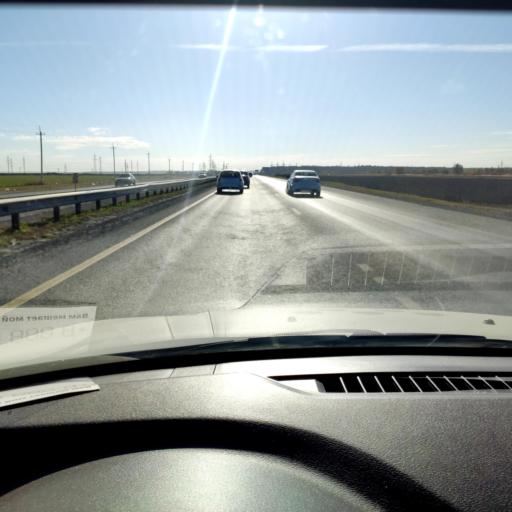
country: RU
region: Samara
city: Zhigulevsk
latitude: 53.5525
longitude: 49.5057
